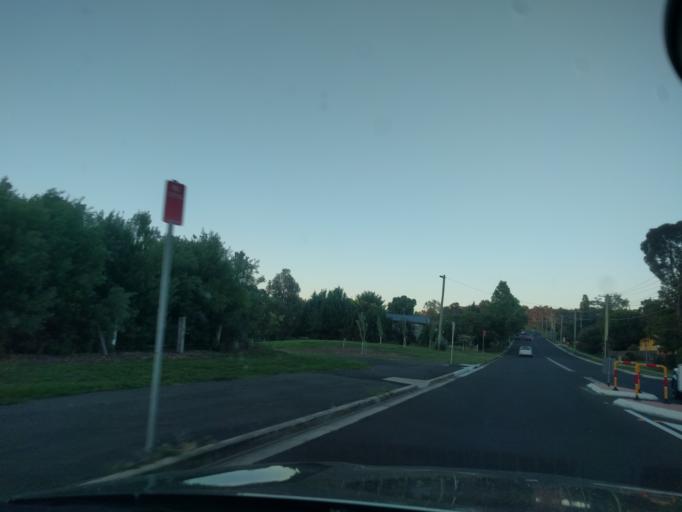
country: AU
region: New South Wales
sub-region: Armidale Dumaresq
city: Armidale
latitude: -30.5083
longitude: 151.6603
